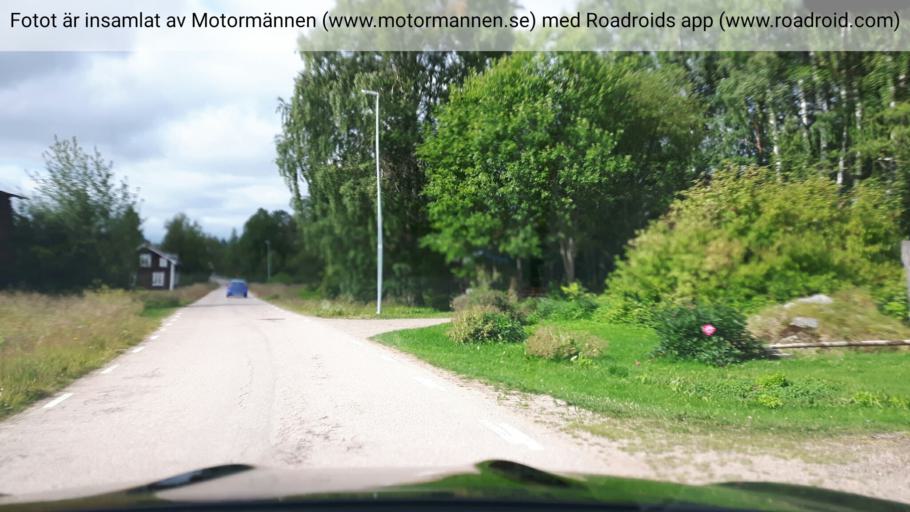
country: SE
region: Jaemtland
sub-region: Harjedalens Kommun
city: Sveg
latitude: 61.7984
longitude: 14.6411
